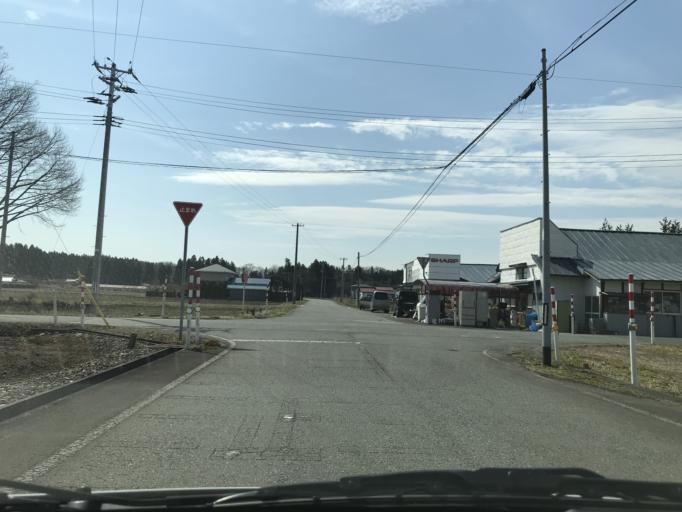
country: JP
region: Iwate
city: Mizusawa
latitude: 39.1226
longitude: 141.0432
